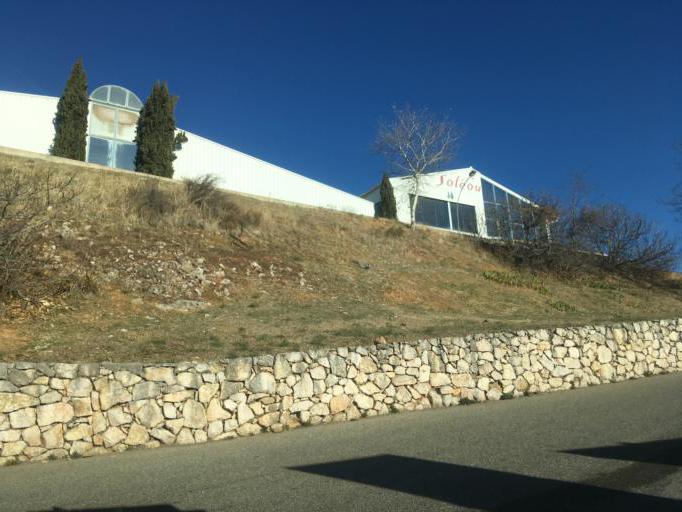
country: FR
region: Provence-Alpes-Cote d'Azur
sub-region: Departement du Var
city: Salernes
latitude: 43.5718
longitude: 6.2198
